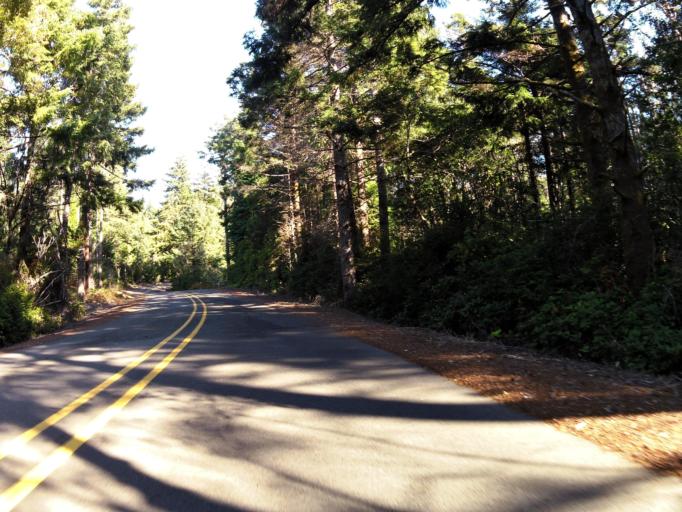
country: US
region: Oregon
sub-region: Coos County
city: Bandon
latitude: 43.0365
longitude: -124.3935
